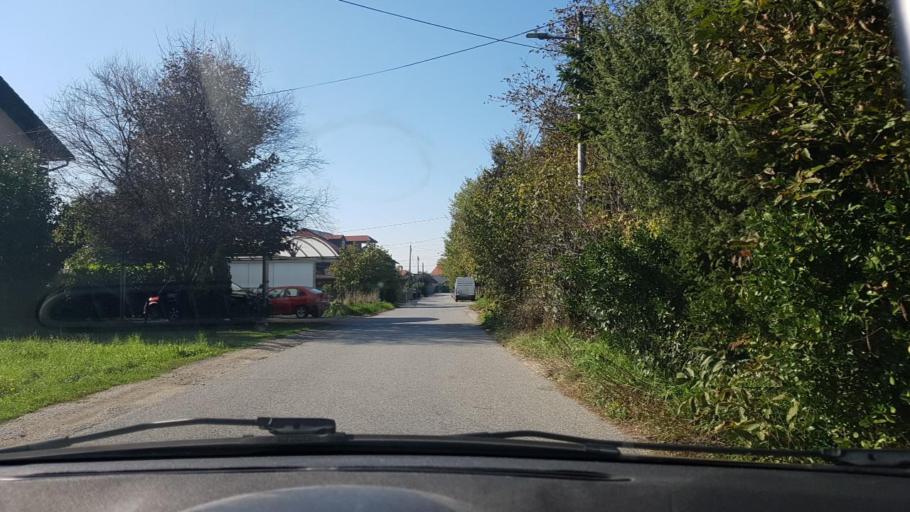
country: HR
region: Grad Zagreb
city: Lucko
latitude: 45.7585
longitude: 15.8863
